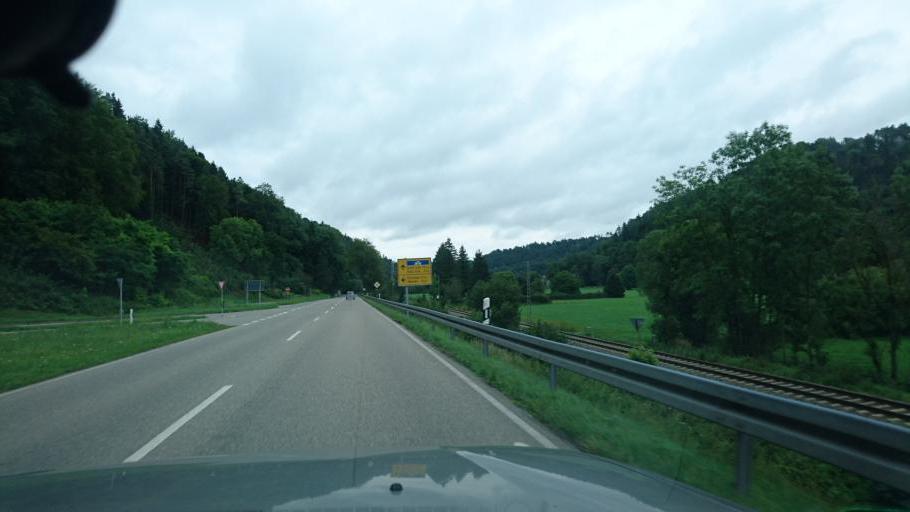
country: DE
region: Baden-Wuerttemberg
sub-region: Freiburg Region
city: Sulz am Neckar
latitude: 48.3563
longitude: 8.6065
